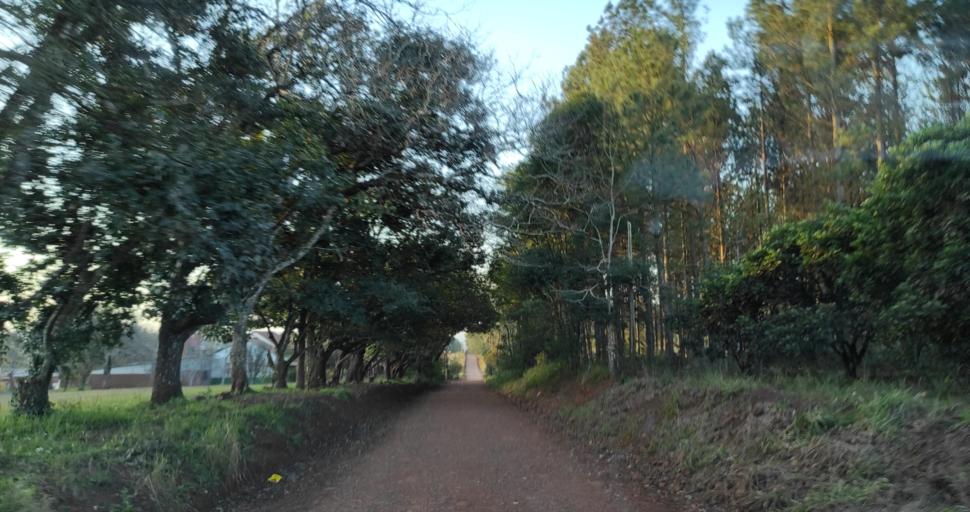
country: AR
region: Misiones
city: Capiovi
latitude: -26.8747
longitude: -55.1078
